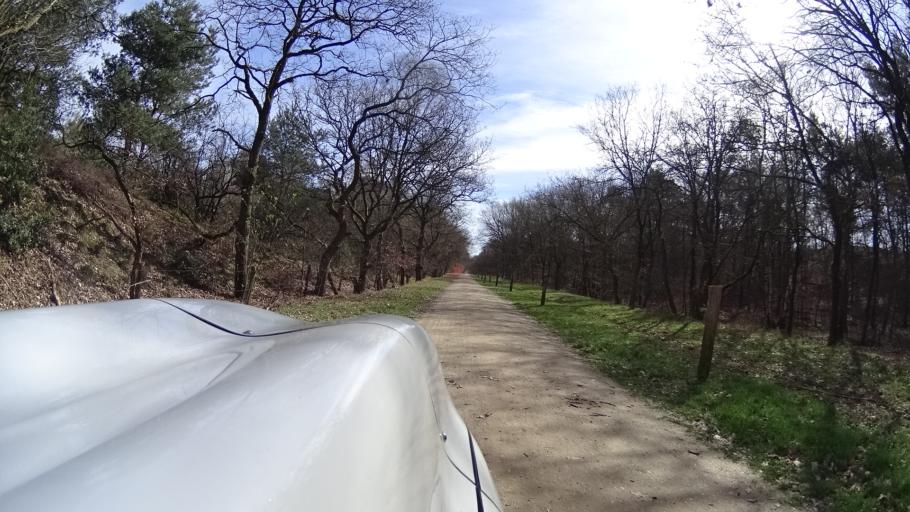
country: NL
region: Limburg
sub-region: Gemeente Gennep
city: Gennep
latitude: 51.6904
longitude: 6.0088
